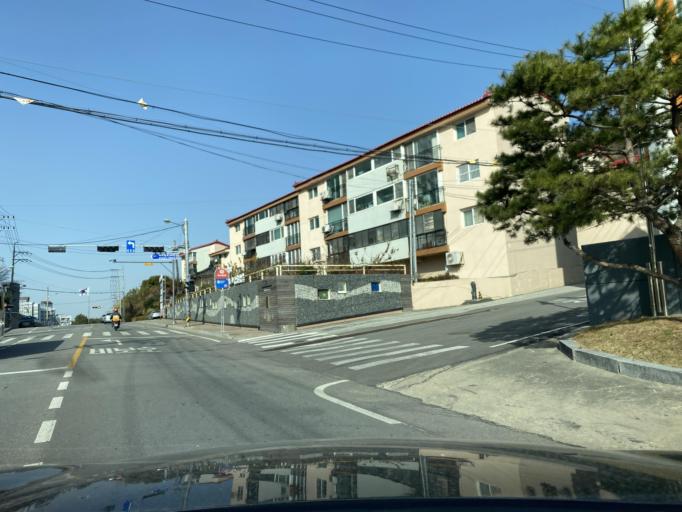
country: KR
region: Chungcheongnam-do
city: Yesan
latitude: 36.6857
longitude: 126.8453
